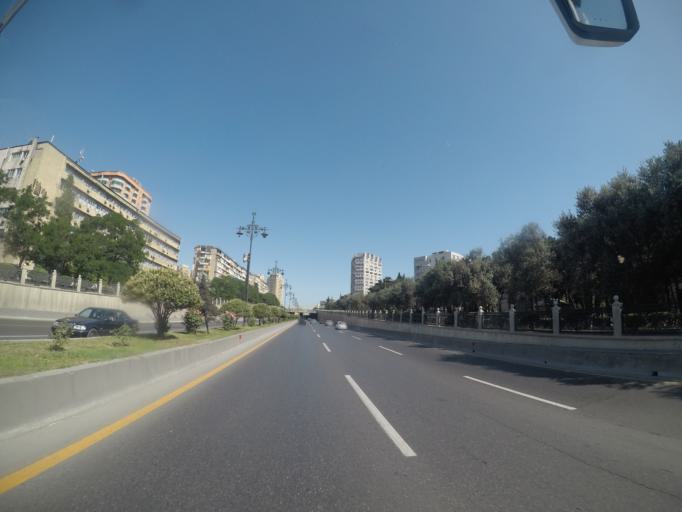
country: AZ
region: Baki
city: Bilajari
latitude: 40.4078
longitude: 49.8056
